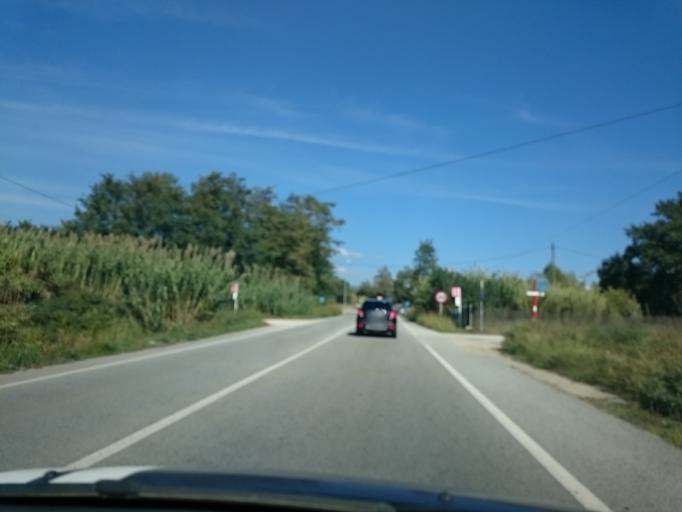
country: ES
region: Catalonia
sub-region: Provincia de Barcelona
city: Les Franqueses del Valles
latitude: 41.6231
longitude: 2.3219
